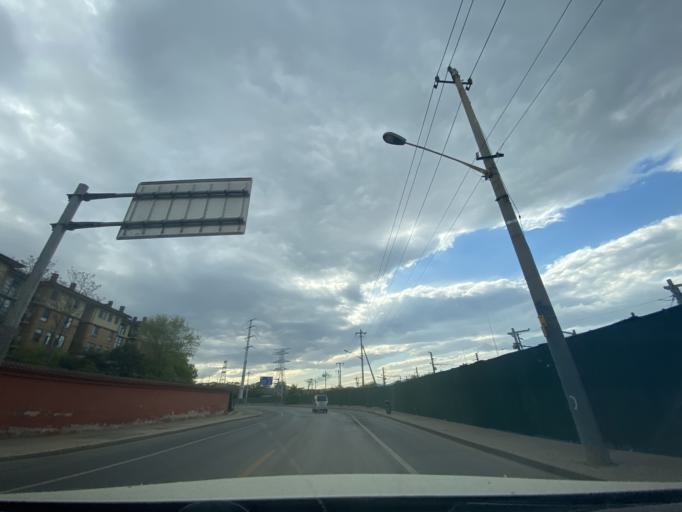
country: CN
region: Beijing
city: Haidian
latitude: 39.9727
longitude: 116.2845
